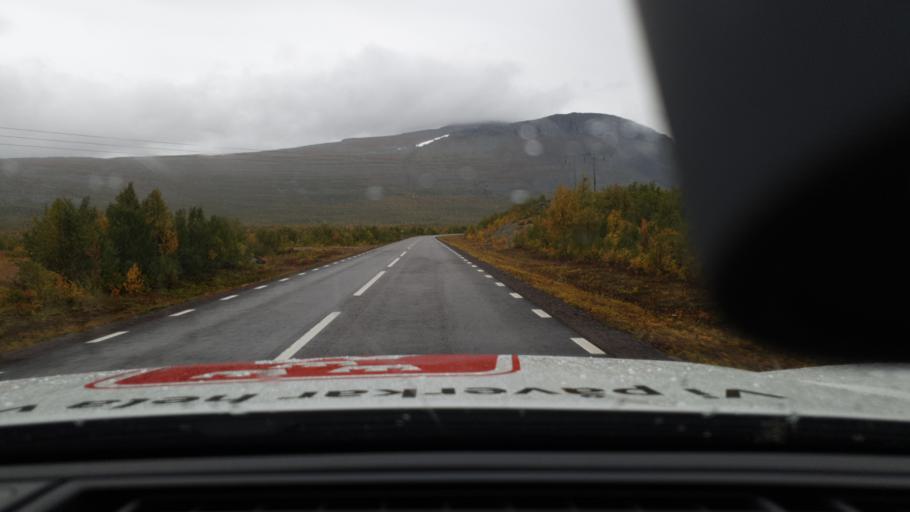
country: SE
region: Norrbotten
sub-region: Kiruna Kommun
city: Kiruna
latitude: 68.2637
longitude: 19.4392
